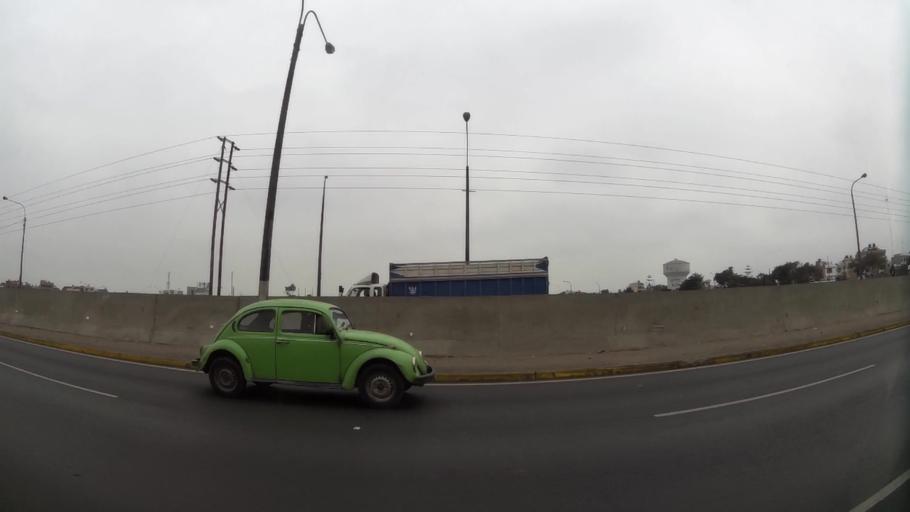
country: PE
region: Lima
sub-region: Lima
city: Independencia
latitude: -11.9613
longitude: -77.0685
